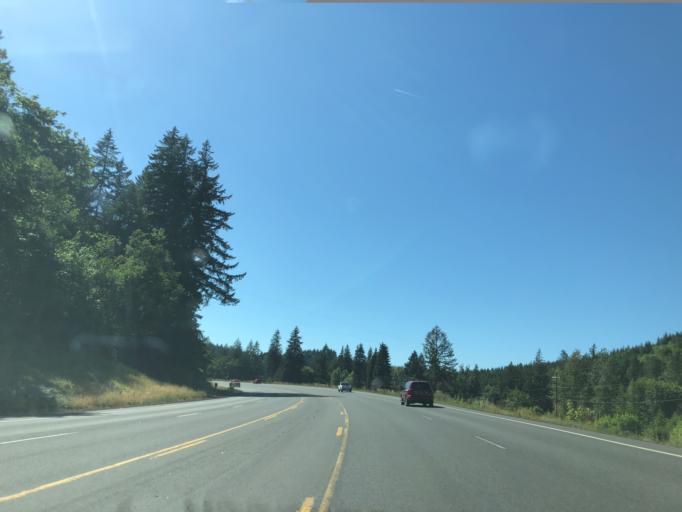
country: US
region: Oregon
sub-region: Linn County
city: Sweet Home
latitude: 44.4043
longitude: -122.7502
